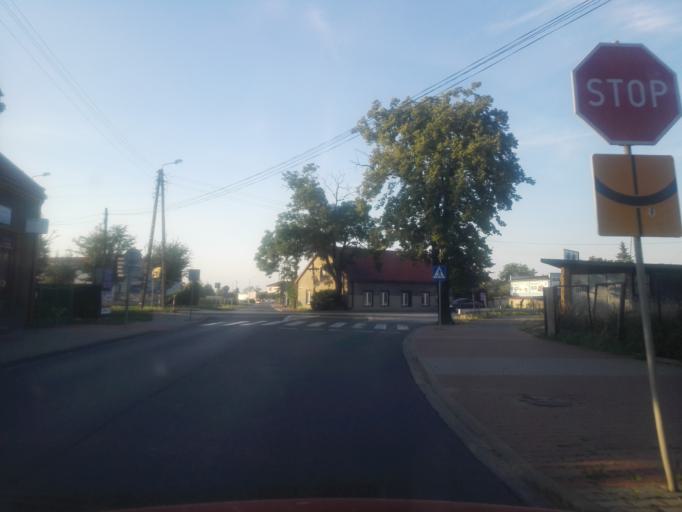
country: PL
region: Lodz Voivodeship
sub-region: Powiat wielunski
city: Wielun
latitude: 51.2227
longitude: 18.5742
